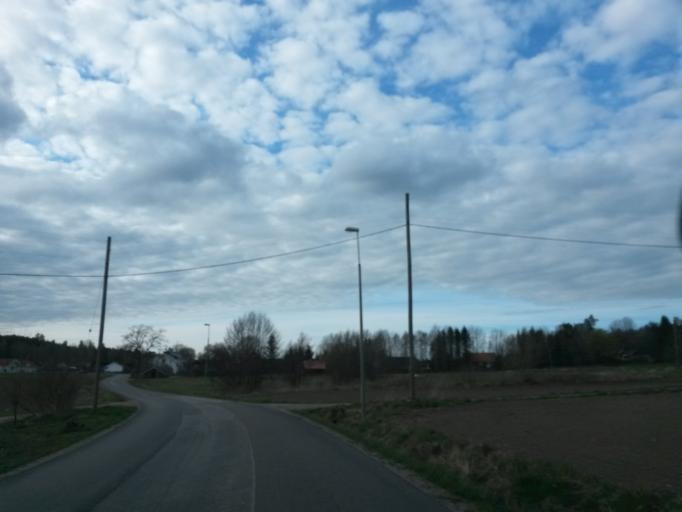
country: SE
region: Vaestra Goetaland
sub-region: Vargarda Kommun
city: Jonstorp
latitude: 58.0204
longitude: 12.6416
